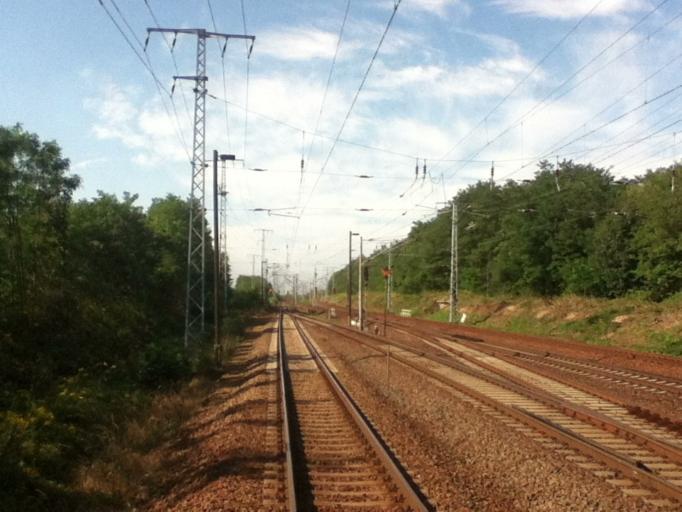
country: DE
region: Brandenburg
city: Senftenberg
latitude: 51.5479
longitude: 14.0448
